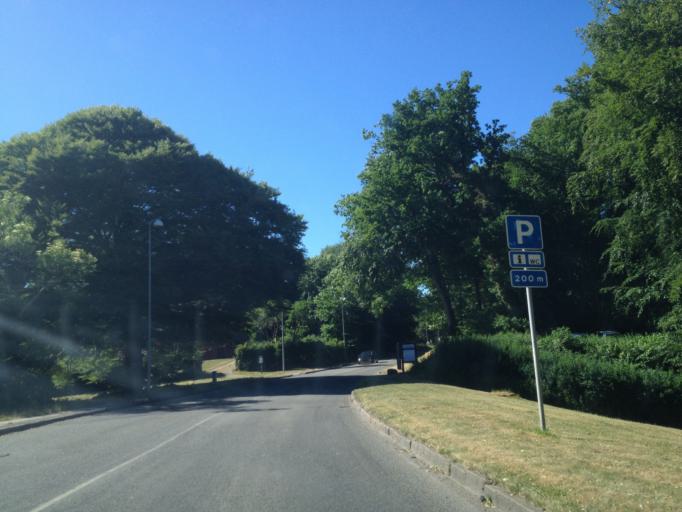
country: DK
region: Capital Region
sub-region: Gentofte Kommune
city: Charlottenlund
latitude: 55.7991
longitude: 12.5875
